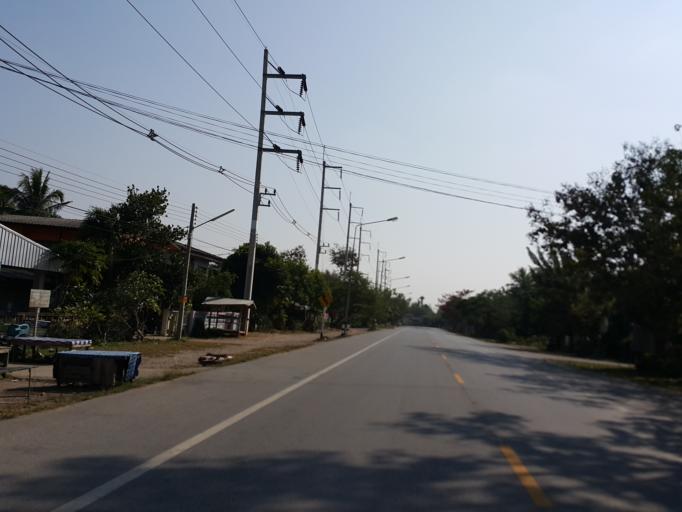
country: TH
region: Lampang
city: Chae Hom
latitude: 18.6742
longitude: 99.5480
